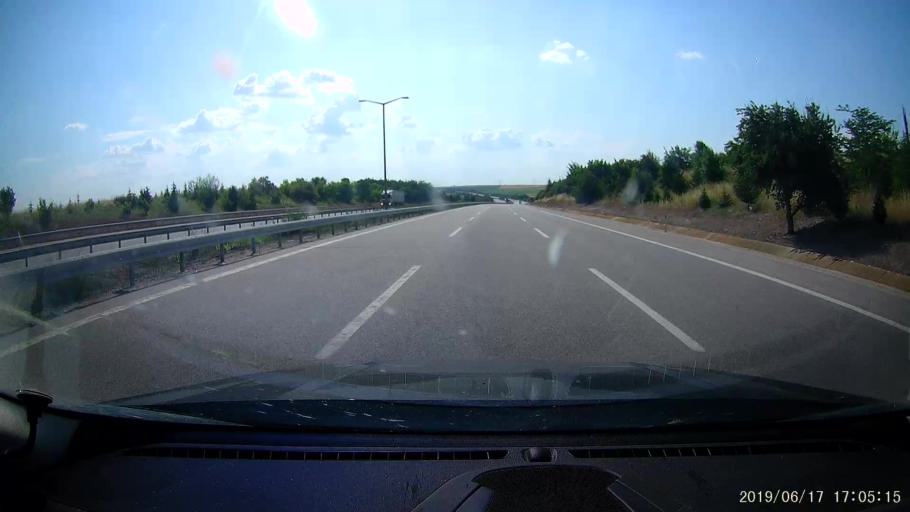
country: TR
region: Edirne
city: Edirne
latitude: 41.6586
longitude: 26.7043
